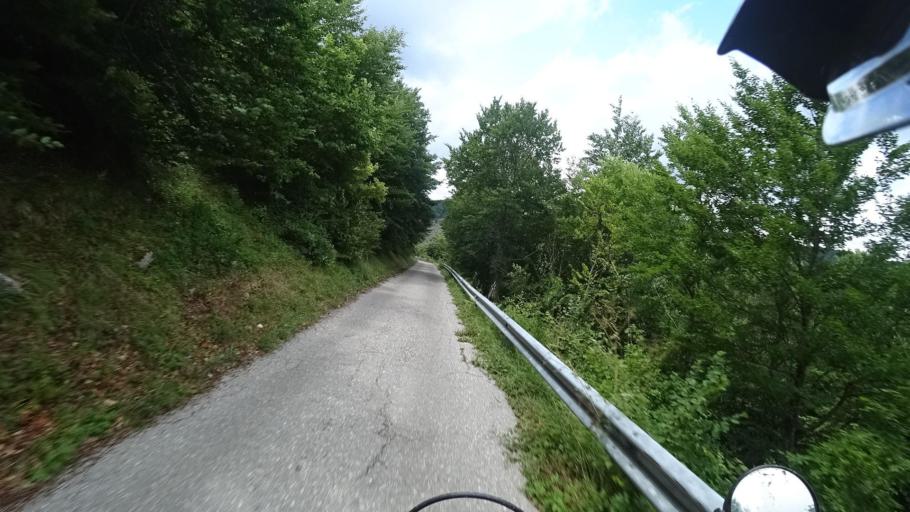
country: HR
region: Licko-Senjska
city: Jezerce
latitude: 44.7415
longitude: 15.4967
